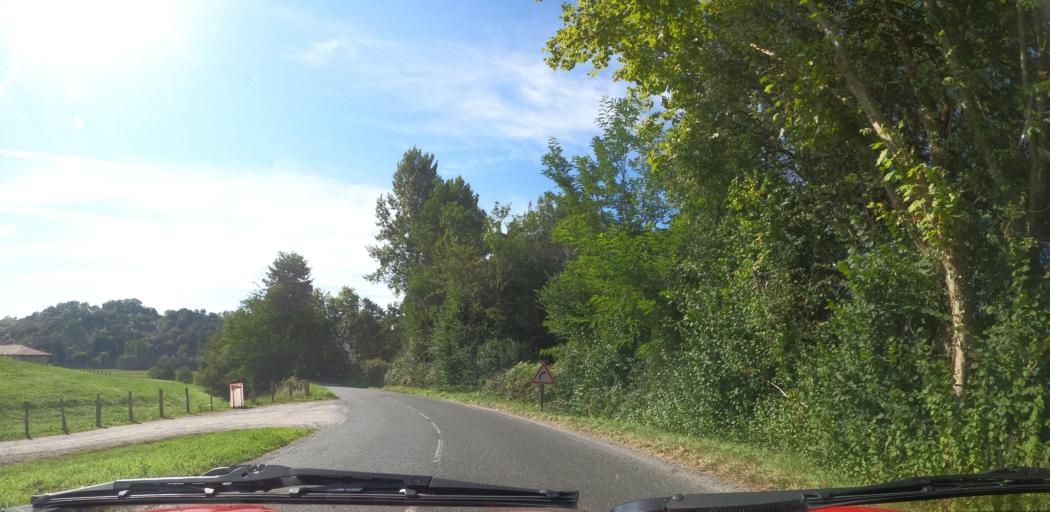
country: FR
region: Aquitaine
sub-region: Departement des Pyrenees-Atlantiques
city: Sare
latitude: 43.3157
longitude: -1.5615
